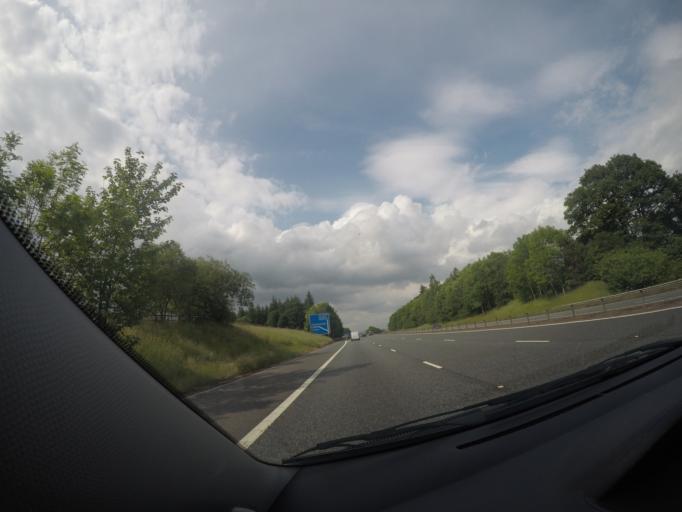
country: GB
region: Scotland
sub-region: Dumfries and Galloway
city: Lochmaben
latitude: 55.2131
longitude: -3.4130
